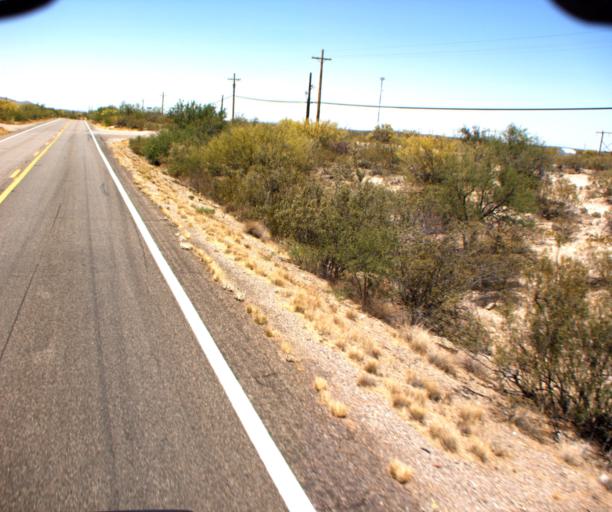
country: US
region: Arizona
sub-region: Pima County
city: Catalina
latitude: 32.6729
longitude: -111.0635
